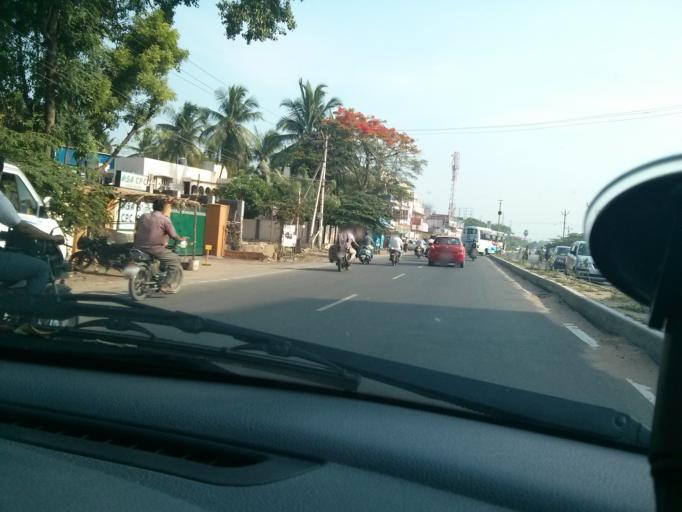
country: IN
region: Tamil Nadu
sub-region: Coimbatore
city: Coimbatore
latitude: 11.0510
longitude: 76.9464
